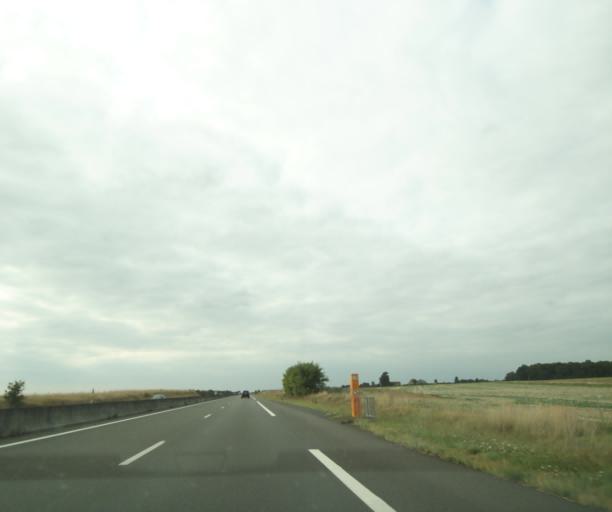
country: FR
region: Centre
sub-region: Departement d'Indre-et-Loire
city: Saint-Paterne-Racan
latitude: 47.6013
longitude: 0.5366
